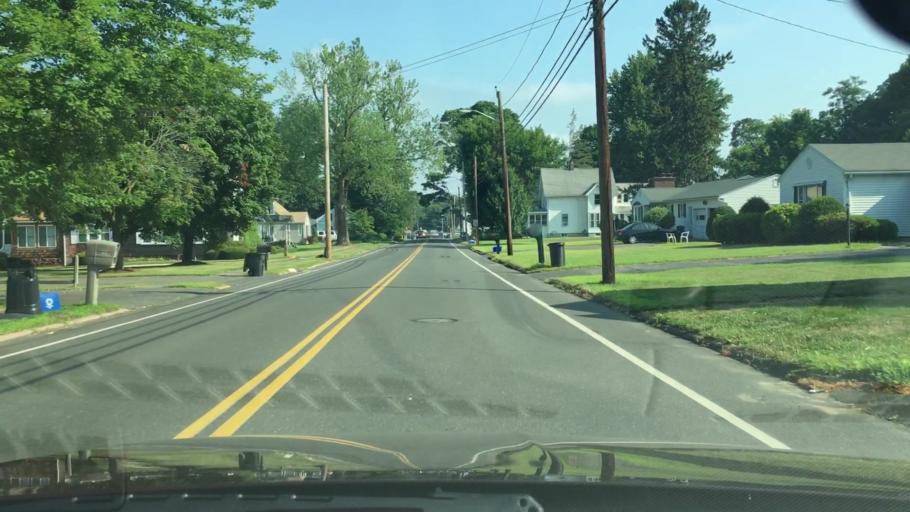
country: US
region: Massachusetts
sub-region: Hampden County
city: East Longmeadow
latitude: 42.0618
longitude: -72.5124
